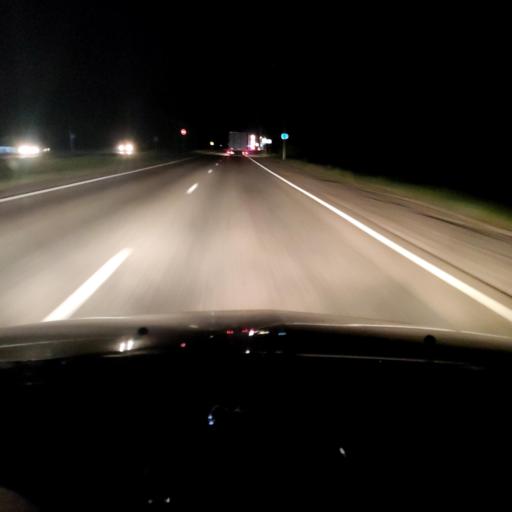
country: RU
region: Belgorod
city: Razumnoye
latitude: 50.6582
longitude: 36.6970
